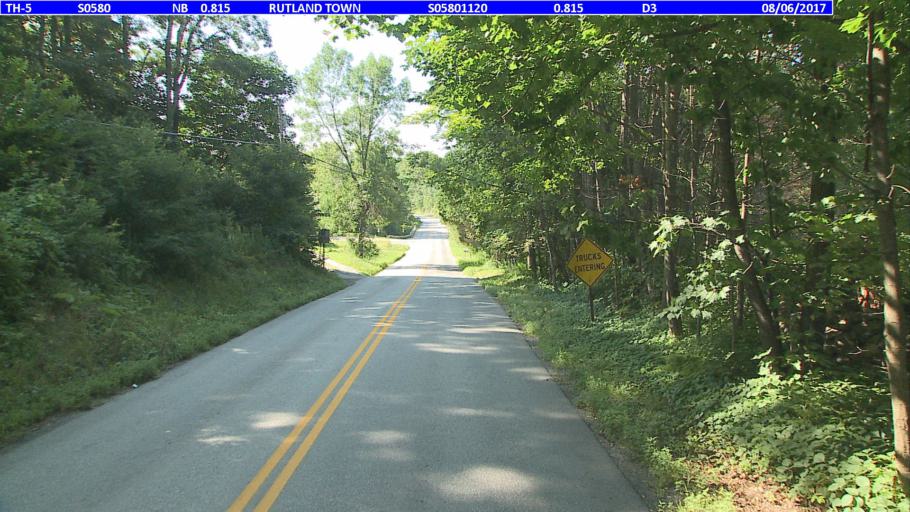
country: US
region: Vermont
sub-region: Rutland County
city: Rutland
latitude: 43.5743
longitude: -72.9515
